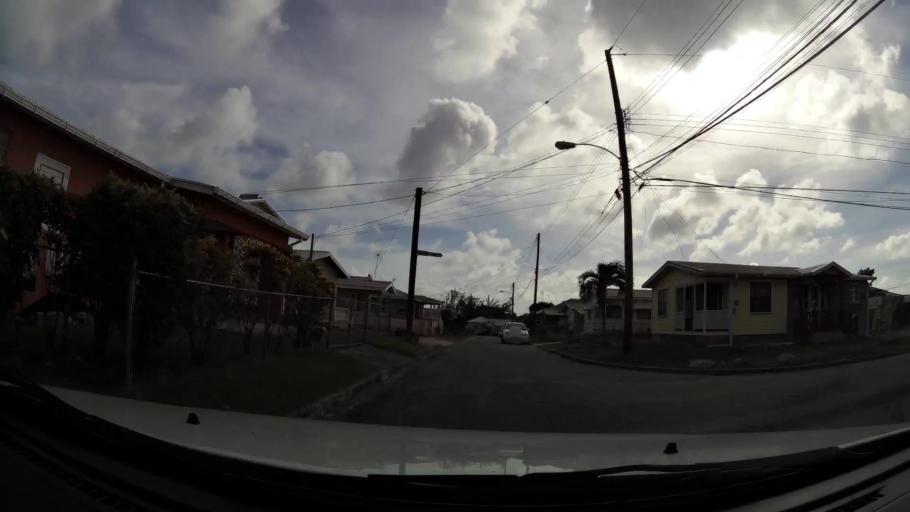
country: BB
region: Saint Michael
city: Bridgetown
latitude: 13.0844
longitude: -59.5816
